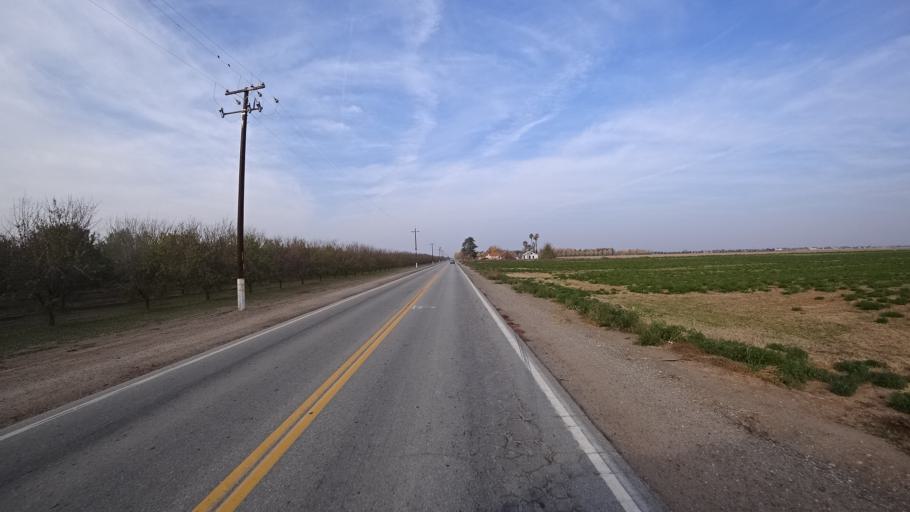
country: US
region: California
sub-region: Kern County
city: Greenacres
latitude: 35.2819
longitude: -119.1283
